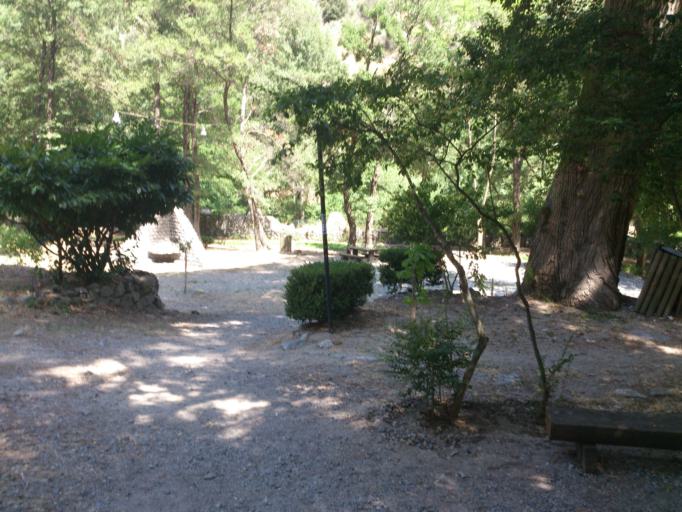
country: IT
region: Calabria
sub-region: Provincia di Reggio Calabria
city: Bivongi
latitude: 38.4861
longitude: 16.4318
